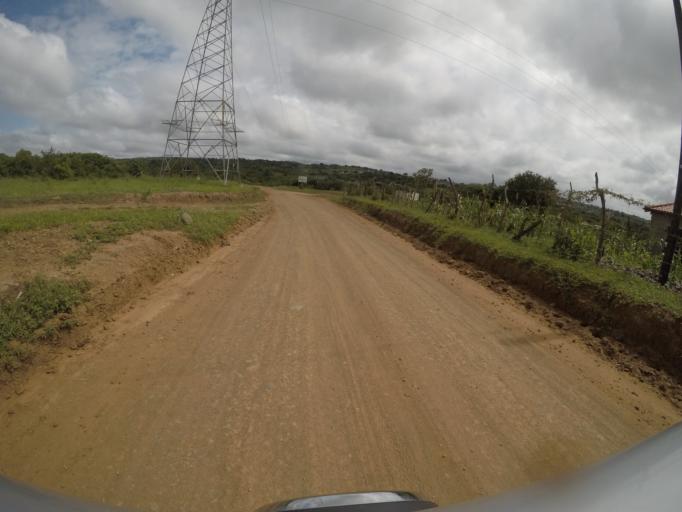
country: ZA
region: KwaZulu-Natal
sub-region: uThungulu District Municipality
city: Empangeni
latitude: -28.5919
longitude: 31.8403
